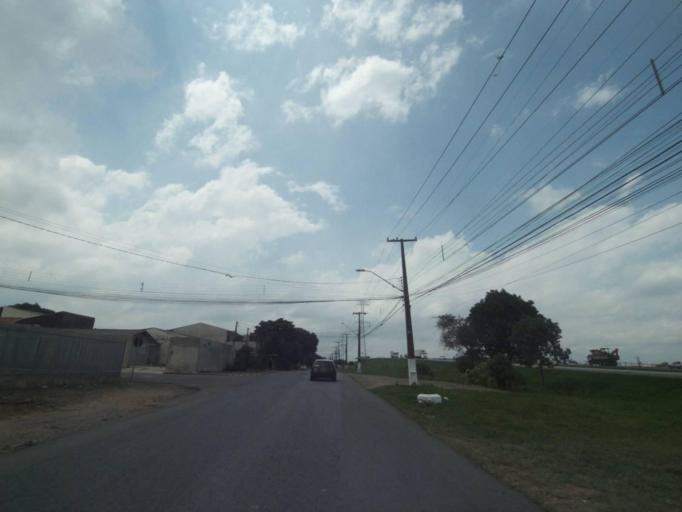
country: BR
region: Parana
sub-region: Curitiba
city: Curitiba
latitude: -25.4864
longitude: -49.3473
